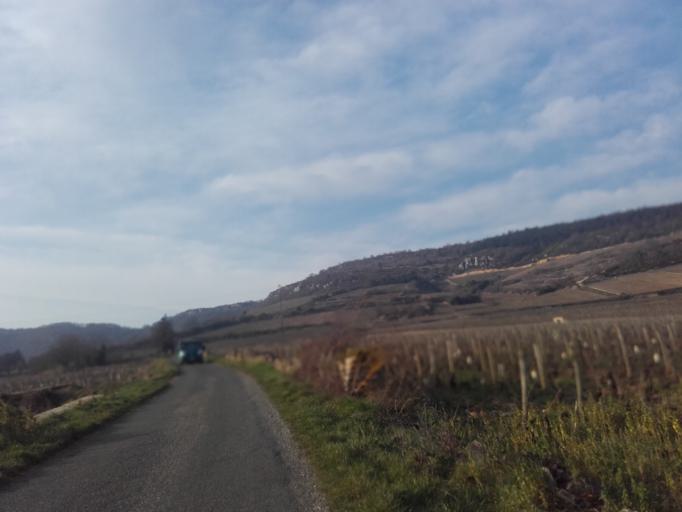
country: FR
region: Bourgogne
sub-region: Departement de Saone-et-Loire
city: Chagny
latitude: 46.9128
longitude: 4.6893
